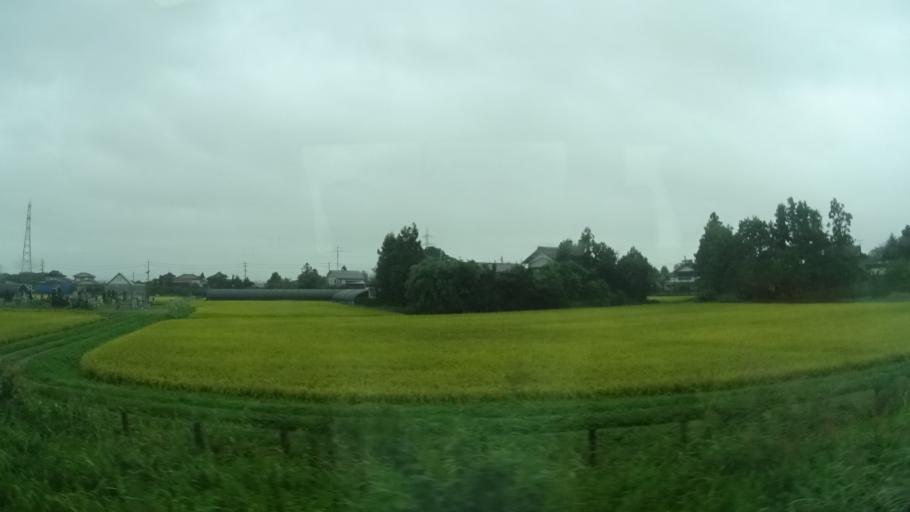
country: JP
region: Yamagata
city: Tsuruoka
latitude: 38.7628
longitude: 139.8876
